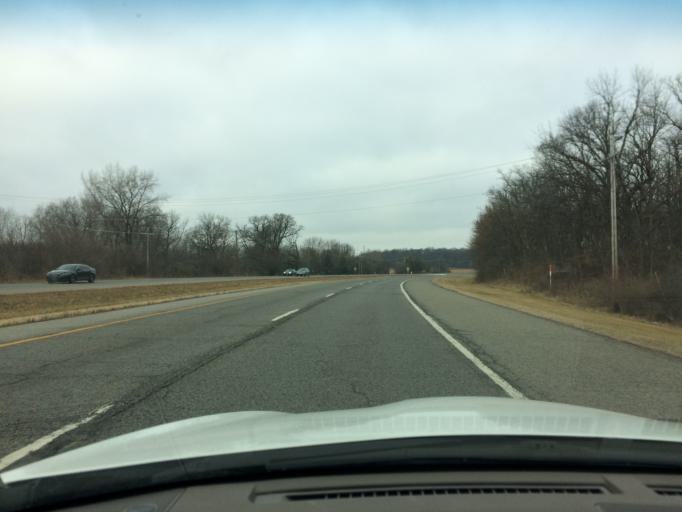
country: US
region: Illinois
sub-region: Kane County
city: Sugar Grove
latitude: 41.7941
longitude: -88.4619
